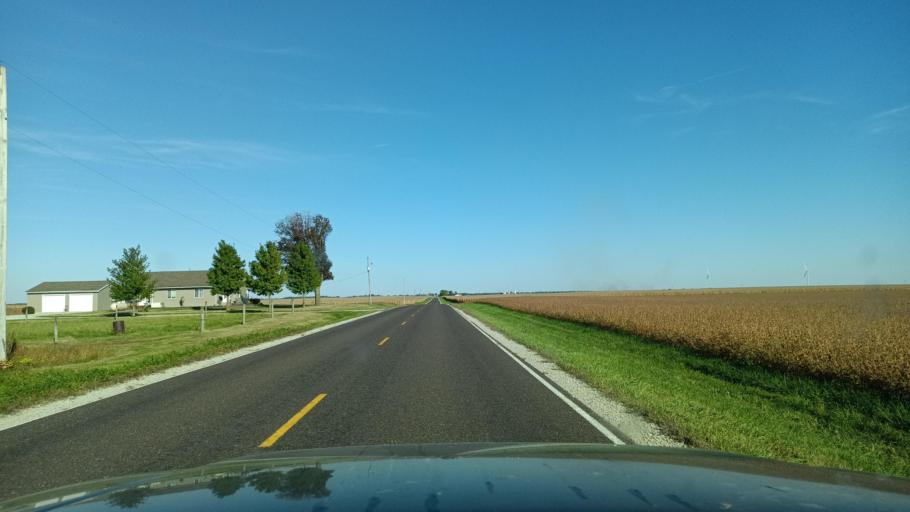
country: US
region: Illinois
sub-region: McLean County
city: Heyworth
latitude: 40.2316
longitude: -89.0507
